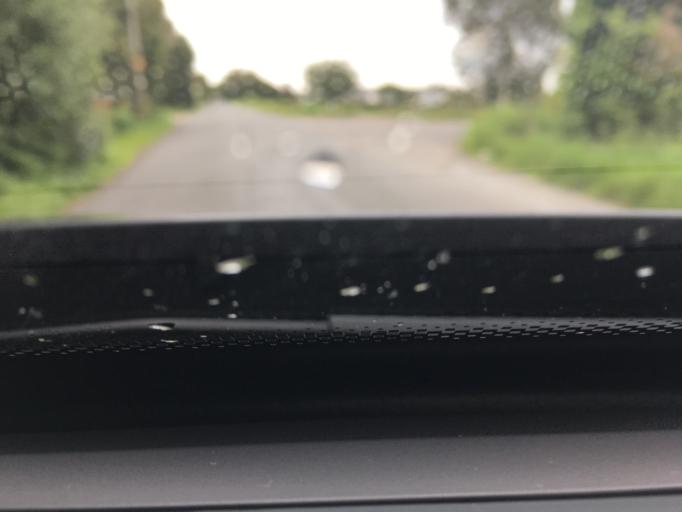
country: GB
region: Northern Ireland
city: Moy
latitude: 54.5134
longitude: -6.6332
